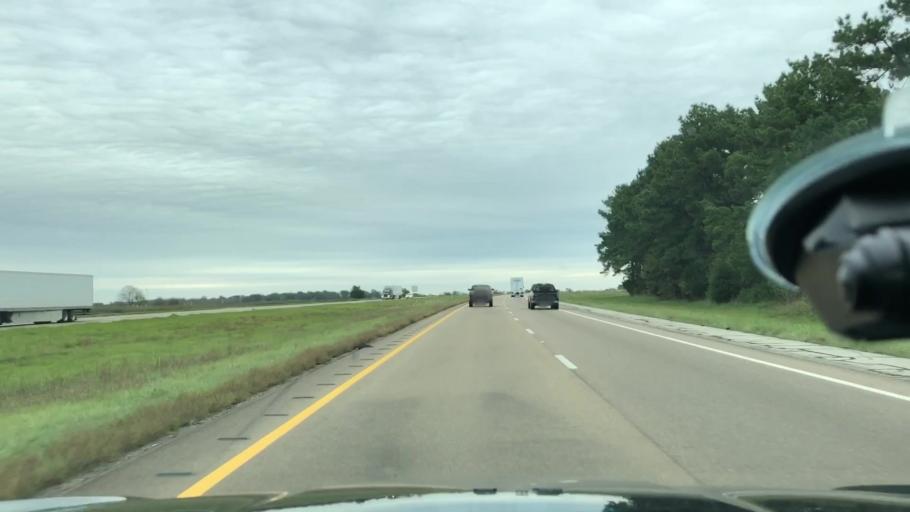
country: US
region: Texas
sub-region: Morris County
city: Omaha
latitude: 33.2864
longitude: -94.7875
